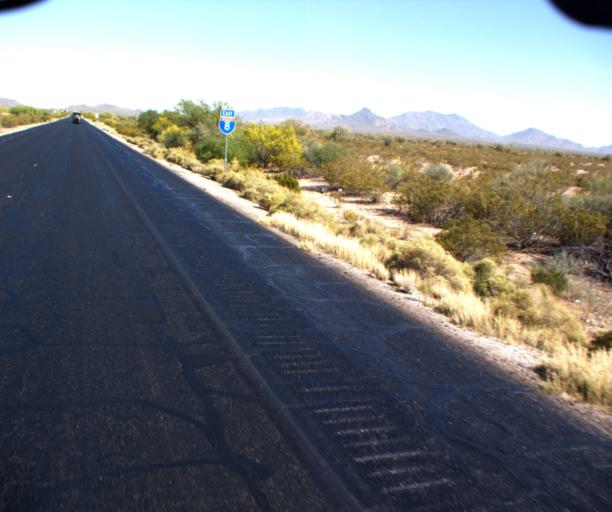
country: US
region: Arizona
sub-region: Pinal County
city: Maricopa
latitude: 32.8414
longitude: -112.2505
